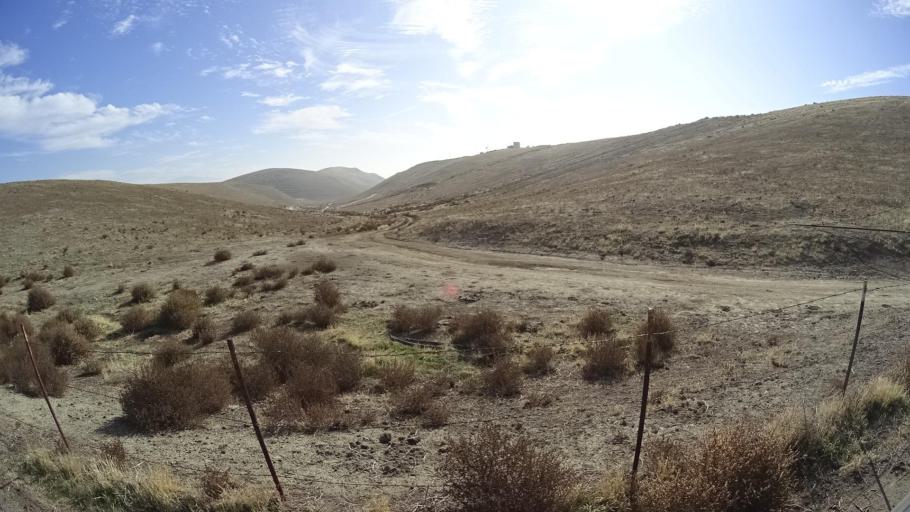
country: US
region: California
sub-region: Kern County
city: Oildale
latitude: 35.4961
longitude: -118.8593
